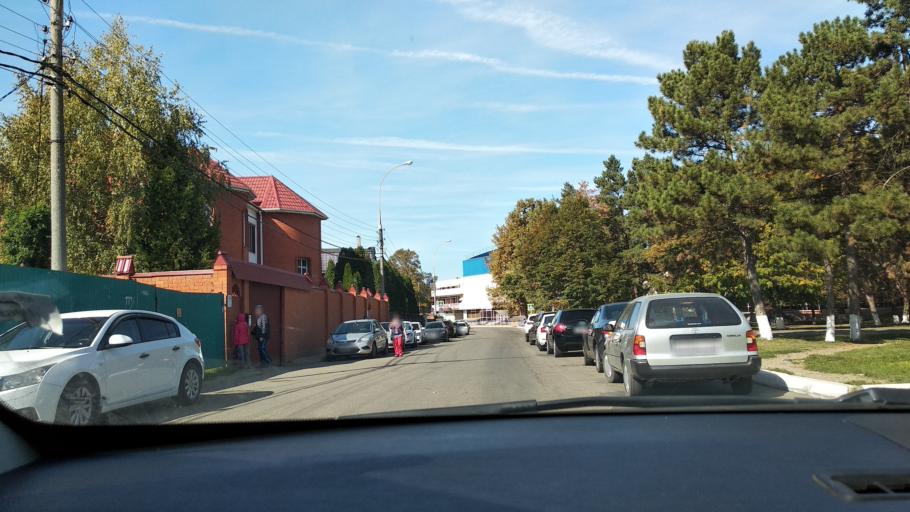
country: RU
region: Adygeya
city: Yablonovskiy
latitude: 45.0152
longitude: 38.9569
